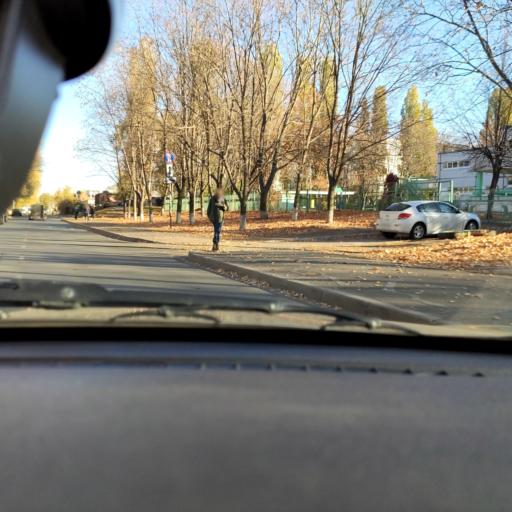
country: RU
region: Samara
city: Tol'yatti
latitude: 53.5253
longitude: 49.2909
